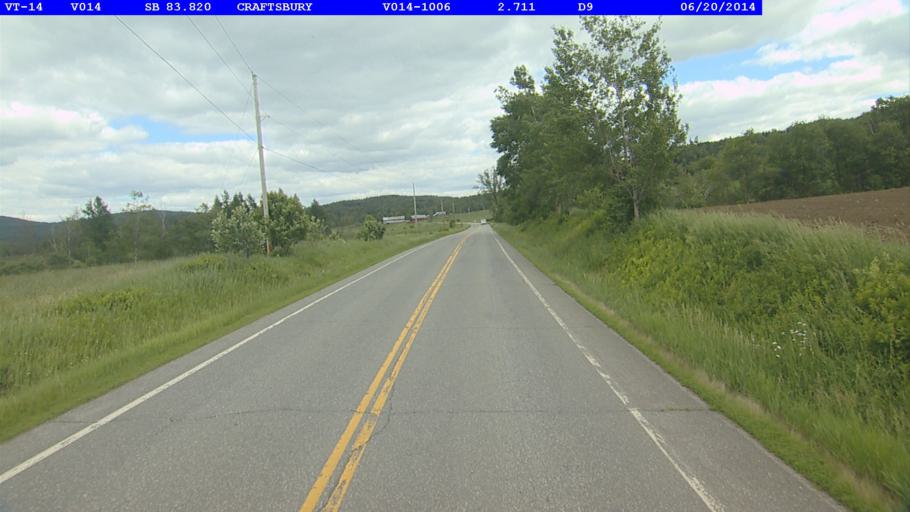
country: US
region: Vermont
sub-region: Caledonia County
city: Hardwick
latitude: 44.6321
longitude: -72.3927
